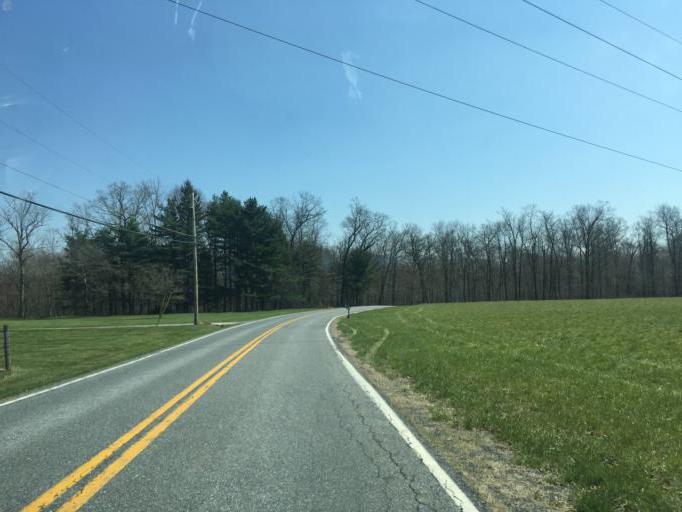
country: US
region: Maryland
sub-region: Washington County
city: Smithsburg
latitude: 39.6208
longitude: -77.5546
